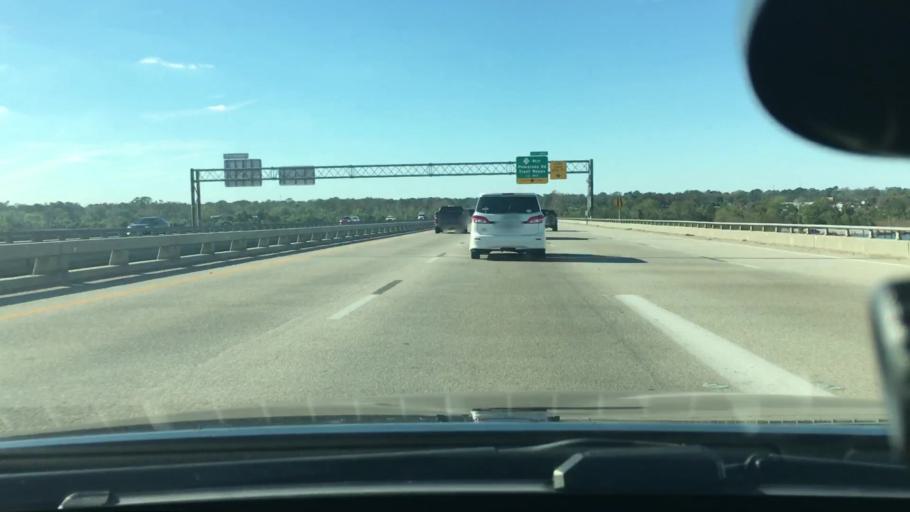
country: US
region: North Carolina
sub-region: Craven County
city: New Bern
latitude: 35.0964
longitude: -77.0457
